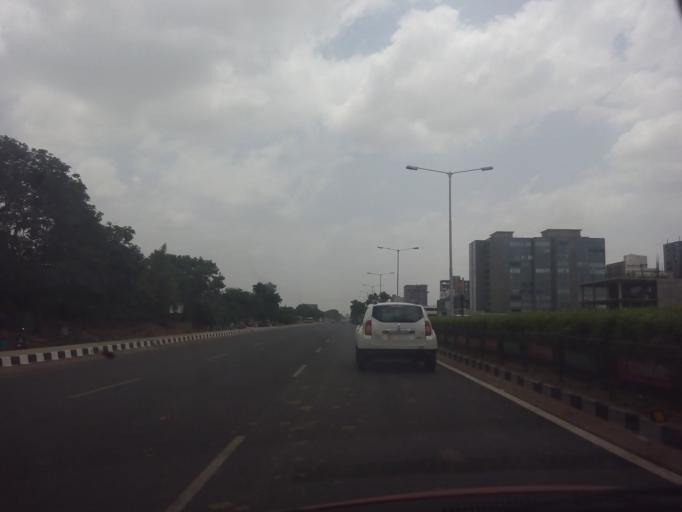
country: IN
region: Gujarat
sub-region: Ahmadabad
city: Sarkhej
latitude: 22.9977
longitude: 72.4981
